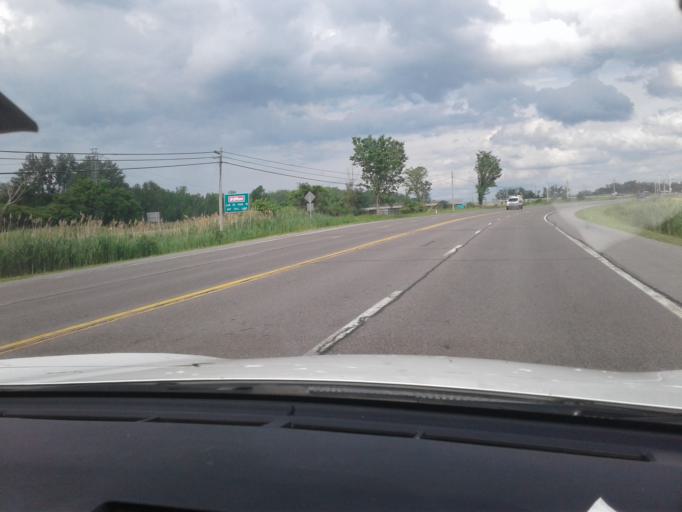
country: US
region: New York
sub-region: Onondaga County
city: East Syracuse
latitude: 43.0937
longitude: -76.0647
